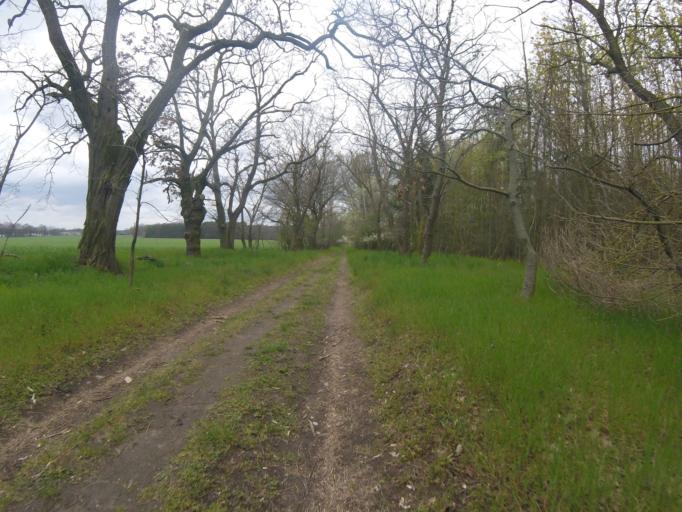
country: DE
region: Brandenburg
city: Mittenwalde
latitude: 52.2486
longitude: 13.5805
